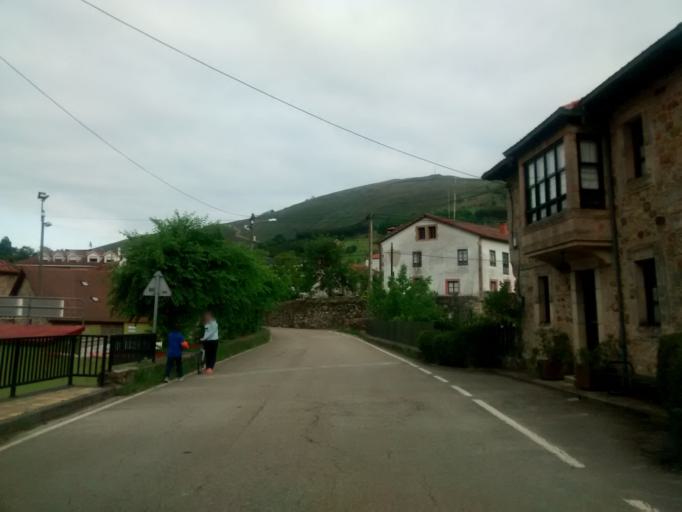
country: ES
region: Cantabria
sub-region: Provincia de Cantabria
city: San Vicente de la Barquera
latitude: 43.2547
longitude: -4.4087
